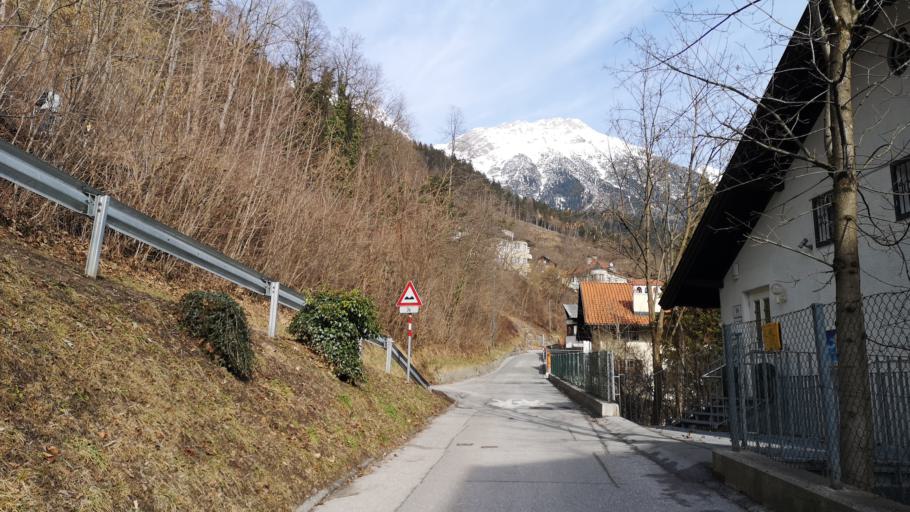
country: AT
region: Tyrol
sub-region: Innsbruck Stadt
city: Innsbruck
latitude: 47.2824
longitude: 11.4050
